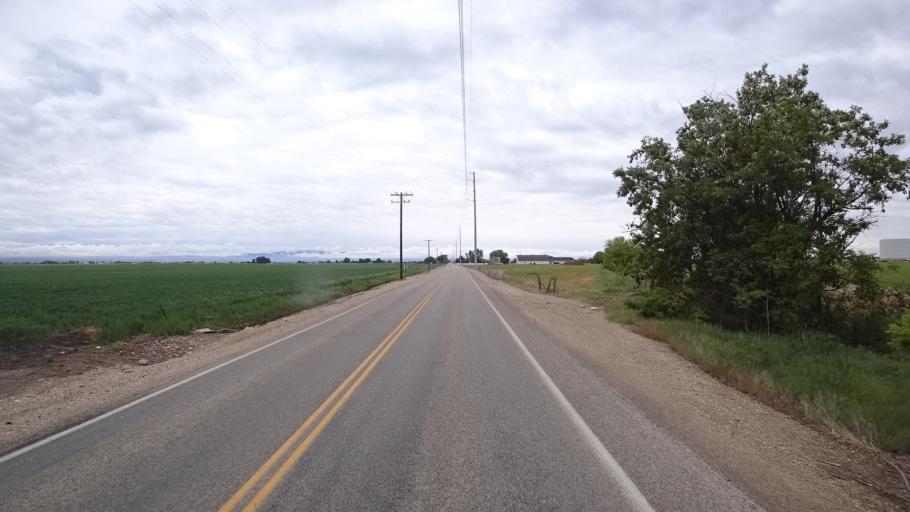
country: US
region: Idaho
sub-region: Ada County
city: Star
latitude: 43.6487
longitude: -116.5126
